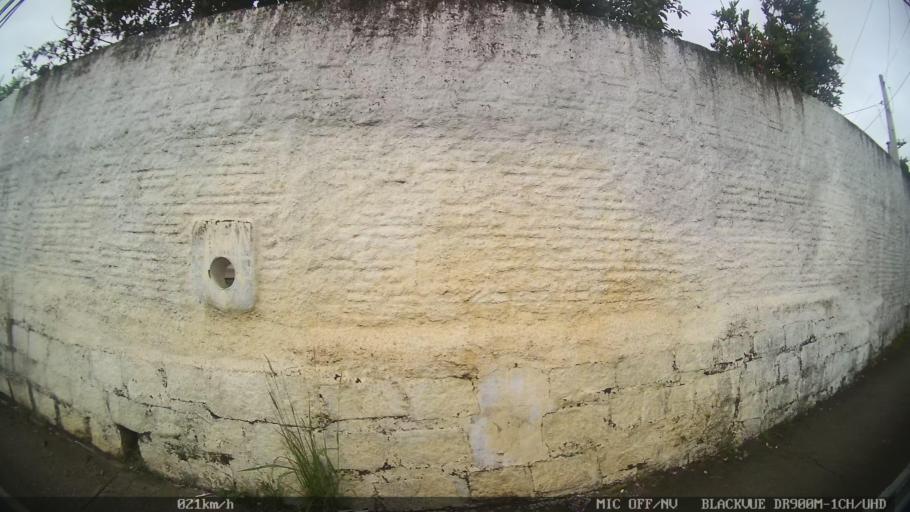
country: BR
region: Santa Catarina
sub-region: Sao Jose
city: Campinas
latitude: -27.5897
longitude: -48.6212
